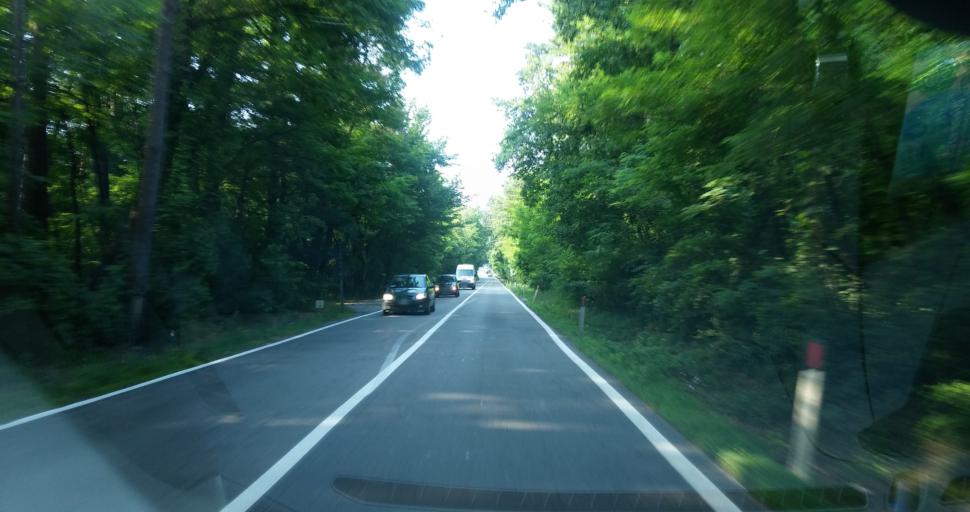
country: IT
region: Lombardy
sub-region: Provincia di Varese
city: Somma Lombardo
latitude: 45.6548
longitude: 8.7042
